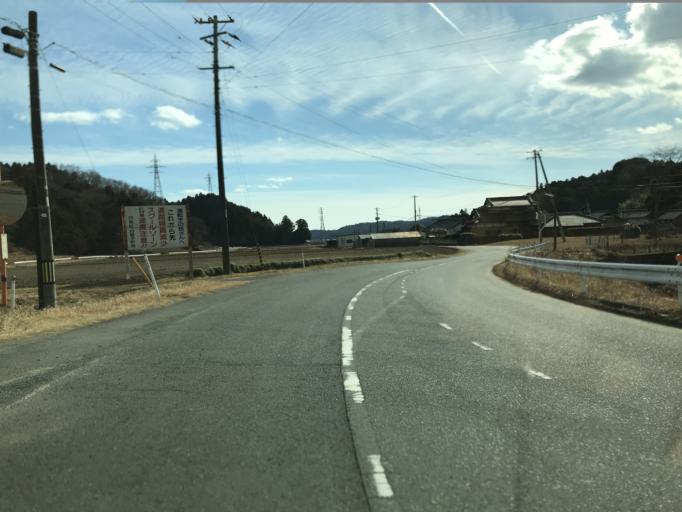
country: JP
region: Fukushima
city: Iwaki
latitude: 37.1286
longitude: 140.9536
